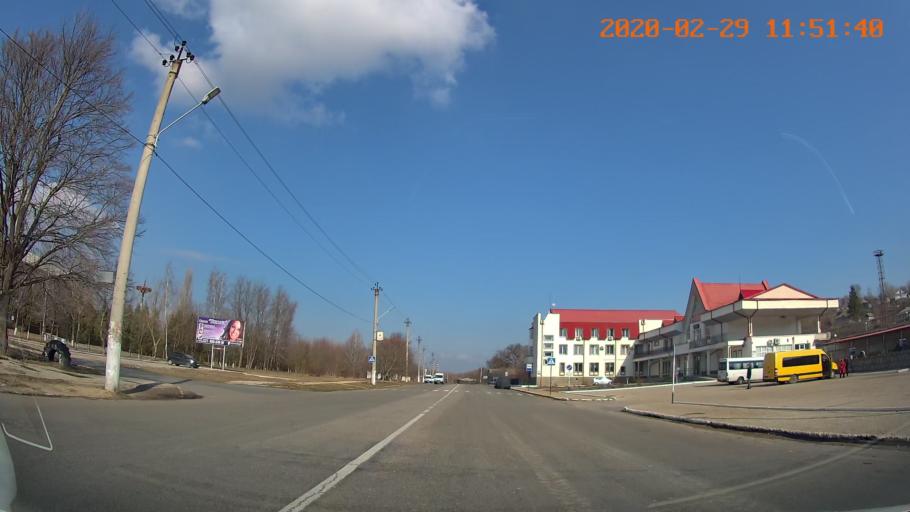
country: MD
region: Telenesti
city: Ribnita
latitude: 47.7657
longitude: 28.9904
